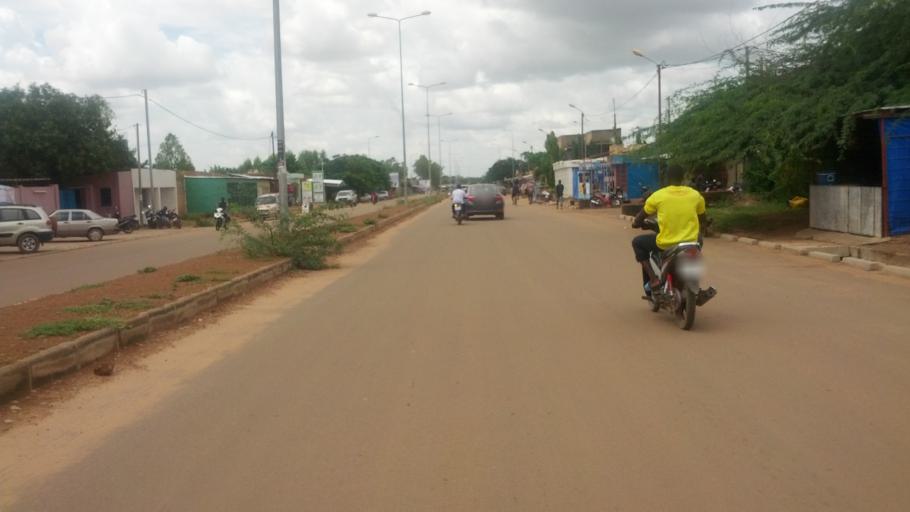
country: BF
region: Centre
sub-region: Kadiogo Province
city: Ouagadougou
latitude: 12.3689
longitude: -1.4977
